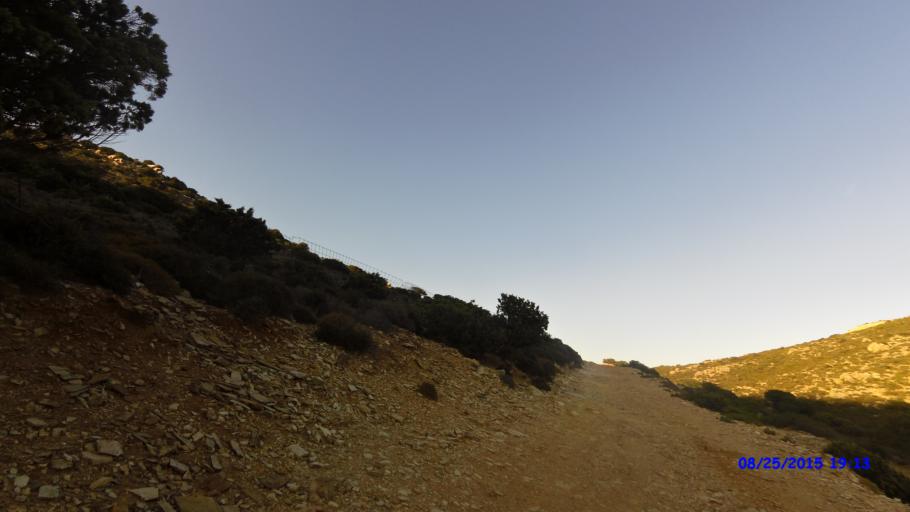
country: GR
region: South Aegean
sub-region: Nomos Kykladon
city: Antiparos
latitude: 36.9961
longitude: 25.0347
